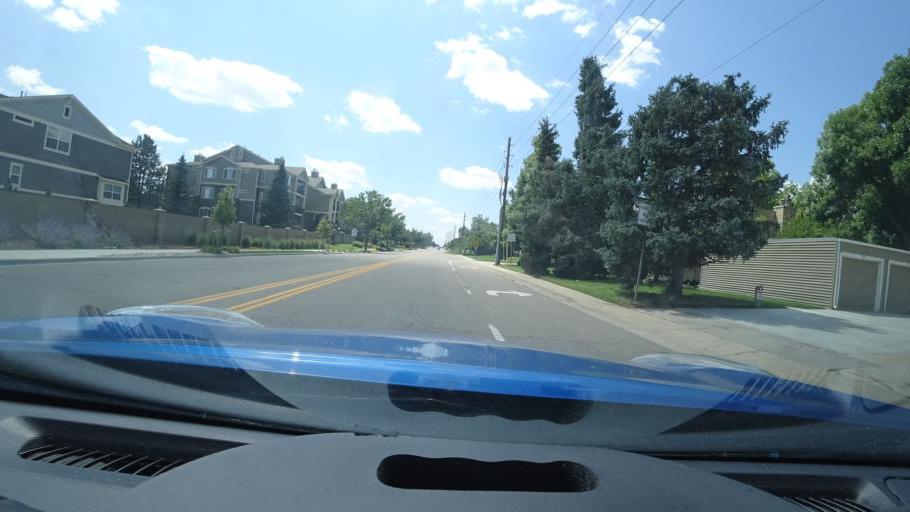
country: US
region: Colorado
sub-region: Adams County
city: Aurora
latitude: 39.6959
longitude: -104.8753
